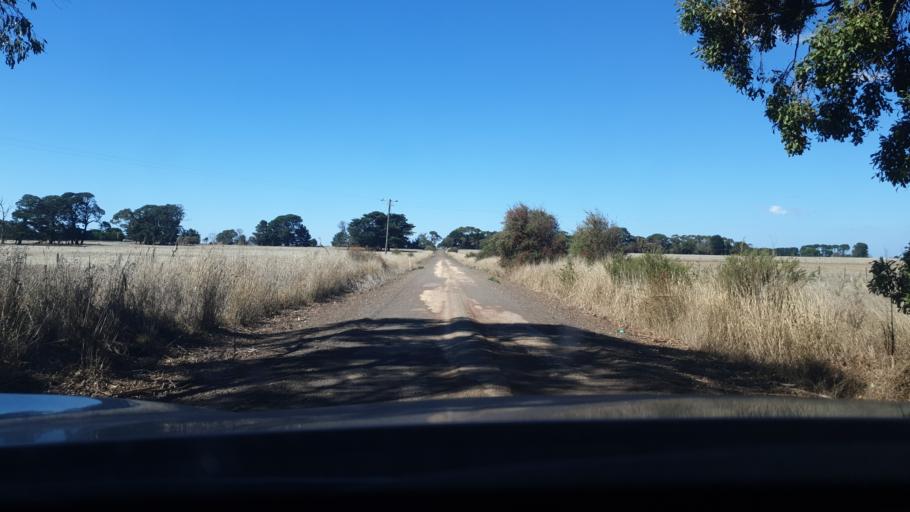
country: AU
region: Victoria
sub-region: Warrnambool
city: Warrnambool
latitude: -38.1648
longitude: 142.3910
